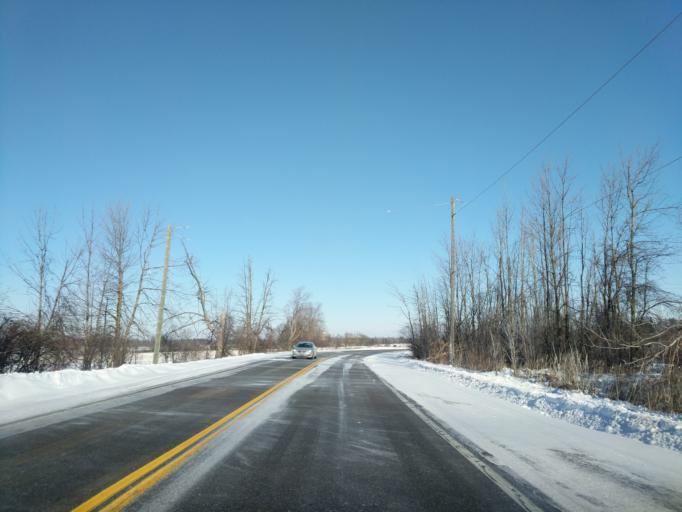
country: CA
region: Ontario
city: Pickering
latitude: 43.8532
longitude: -79.1307
